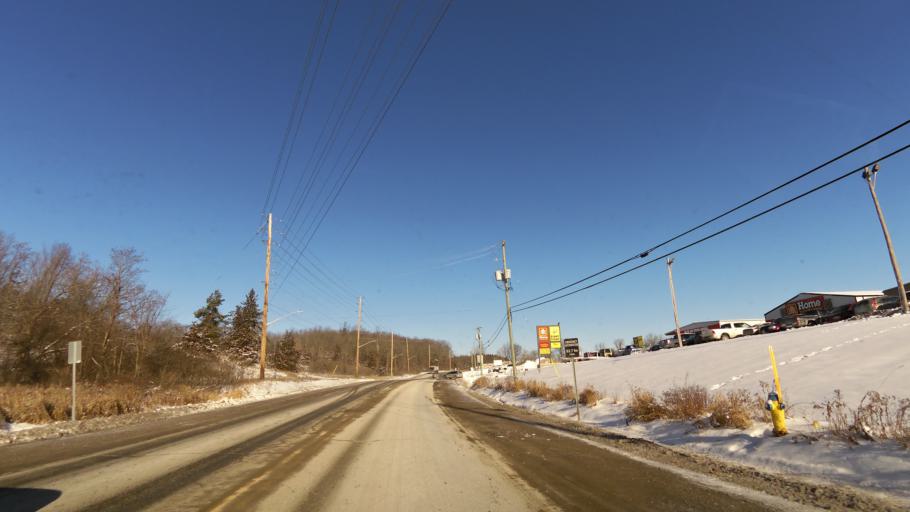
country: CA
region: Ontario
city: Quinte West
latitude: 44.2855
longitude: -77.8097
